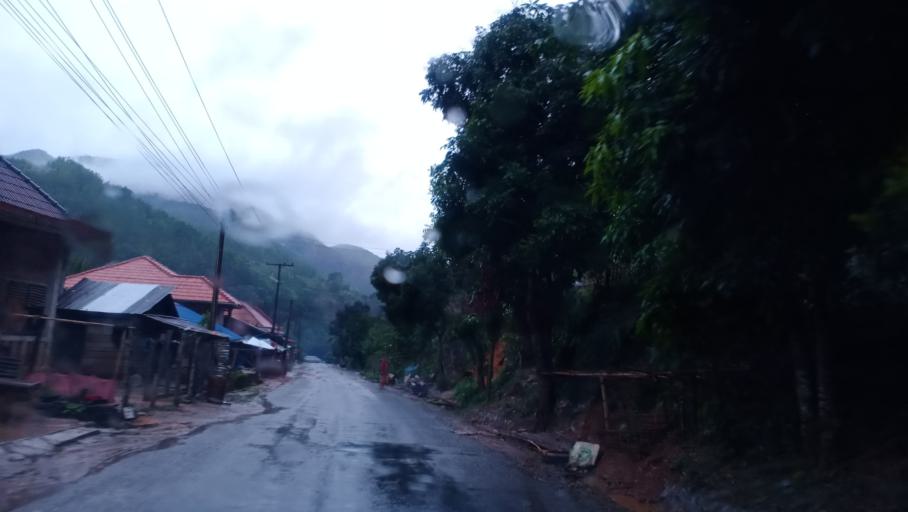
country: LA
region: Phongsali
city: Khoa
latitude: 21.0681
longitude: 102.4901
